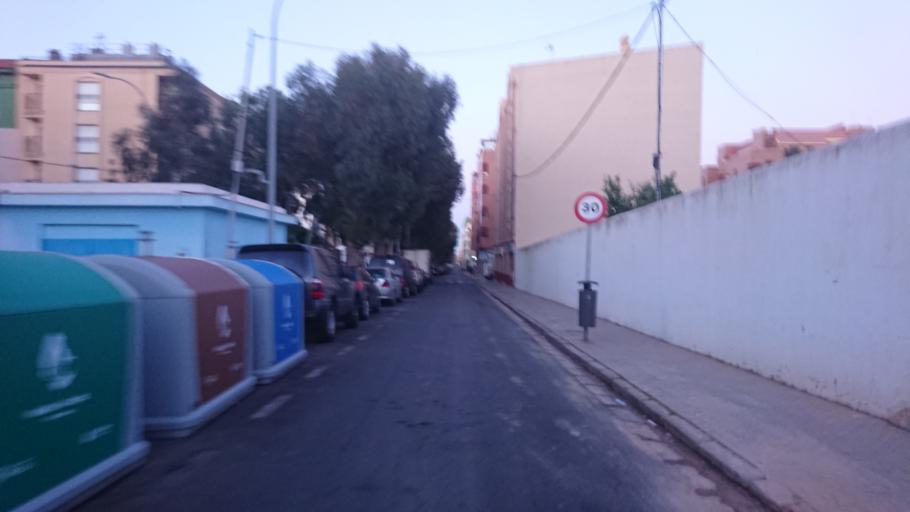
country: ES
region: Melilla
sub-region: Melilla
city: Melilla
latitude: 35.2729
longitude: -2.9465
